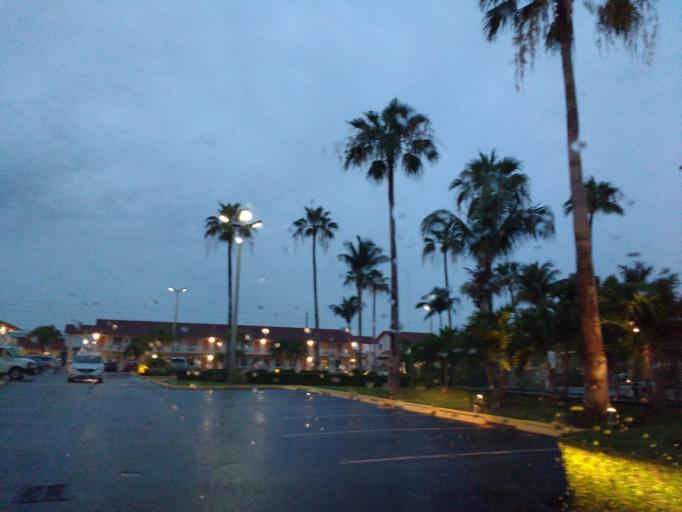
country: US
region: Florida
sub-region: Miami-Dade County
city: Florida City
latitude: 25.4461
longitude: -80.4761
